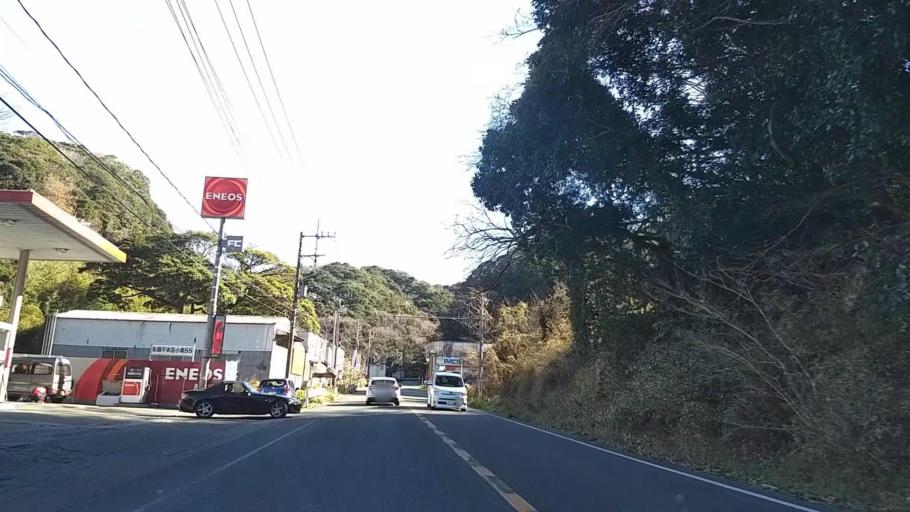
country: JP
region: Chiba
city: Kawaguchi
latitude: 35.1202
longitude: 140.2033
